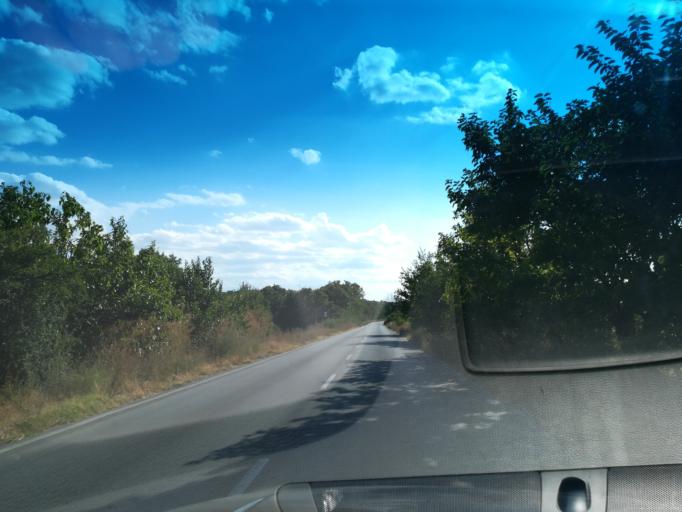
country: BG
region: Khaskovo
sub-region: Obshtina Mineralni Bani
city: Mineralni Bani
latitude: 42.0189
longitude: 25.4104
